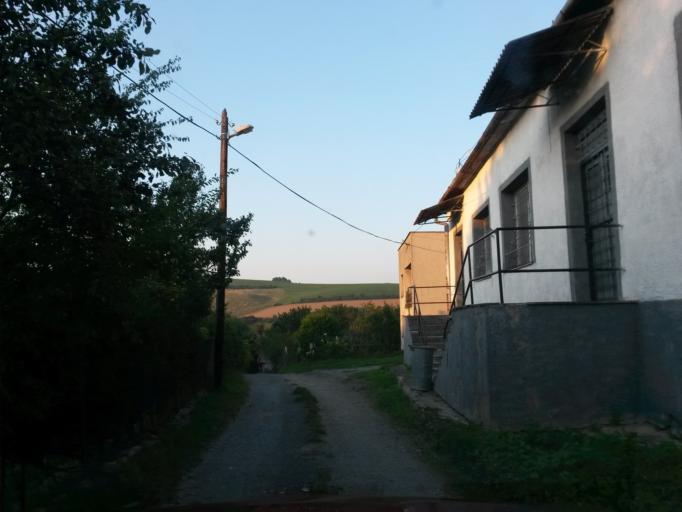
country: SK
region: Presovsky
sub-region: Okres Presov
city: Presov
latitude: 48.9239
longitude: 21.1885
